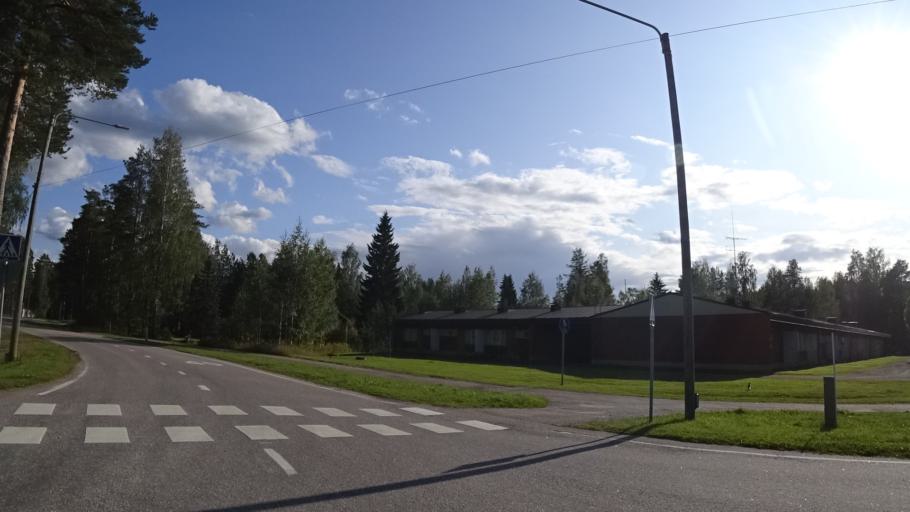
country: FI
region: North Karelia
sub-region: Keski-Karjala
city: Kesaelahti
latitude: 61.8912
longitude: 29.8373
